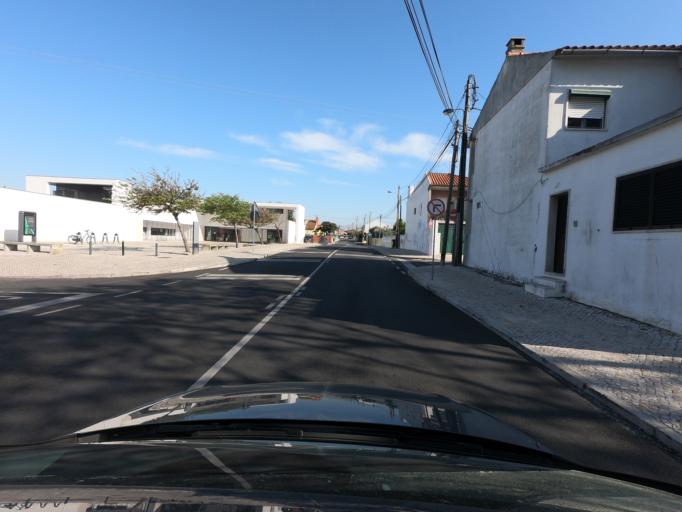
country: PT
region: Lisbon
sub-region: Cascais
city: Sao Domingos de Rana
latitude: 38.7189
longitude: -9.3425
